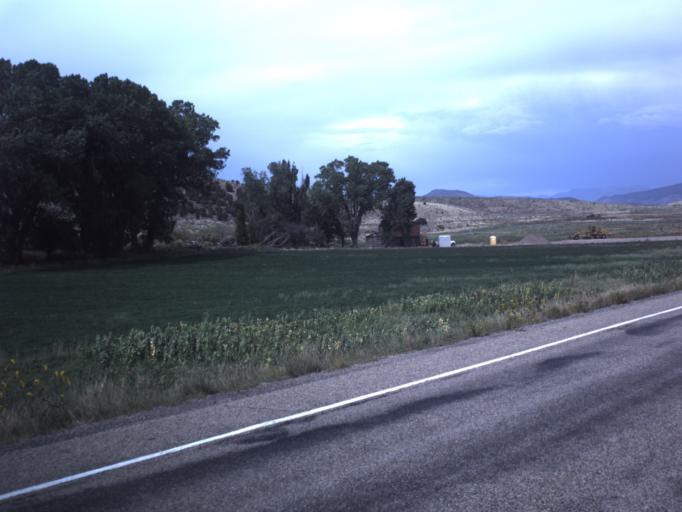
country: US
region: Utah
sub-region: Piute County
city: Junction
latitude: 38.1429
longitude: -112.3059
